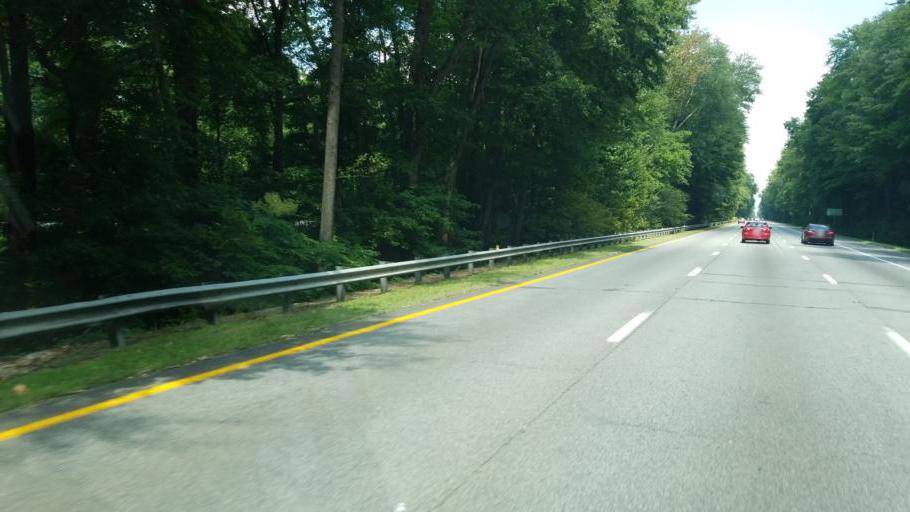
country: US
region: Virginia
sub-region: City of Suffolk
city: Suffolk
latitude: 36.7665
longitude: -76.4757
